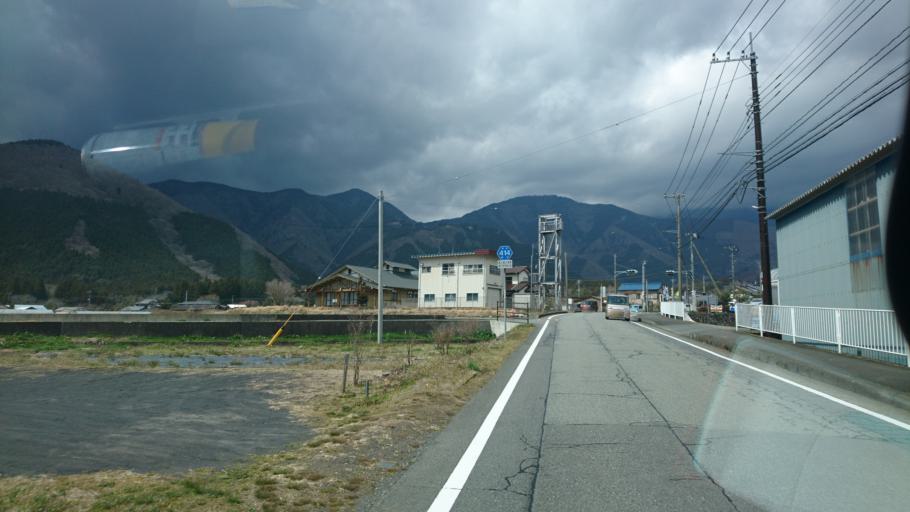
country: JP
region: Shizuoka
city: Fujinomiya
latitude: 35.3611
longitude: 138.5649
